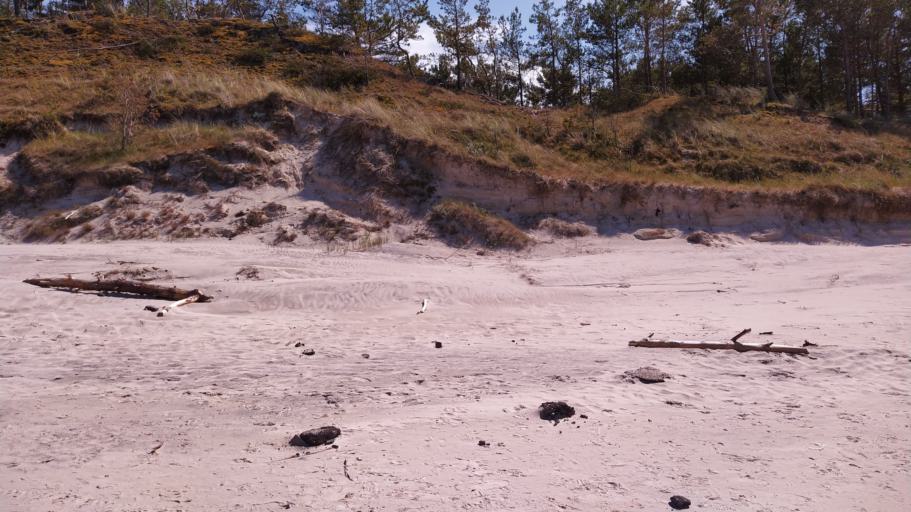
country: PL
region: Pomeranian Voivodeship
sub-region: Powiat leborski
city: Leba
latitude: 54.7565
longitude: 17.4718
